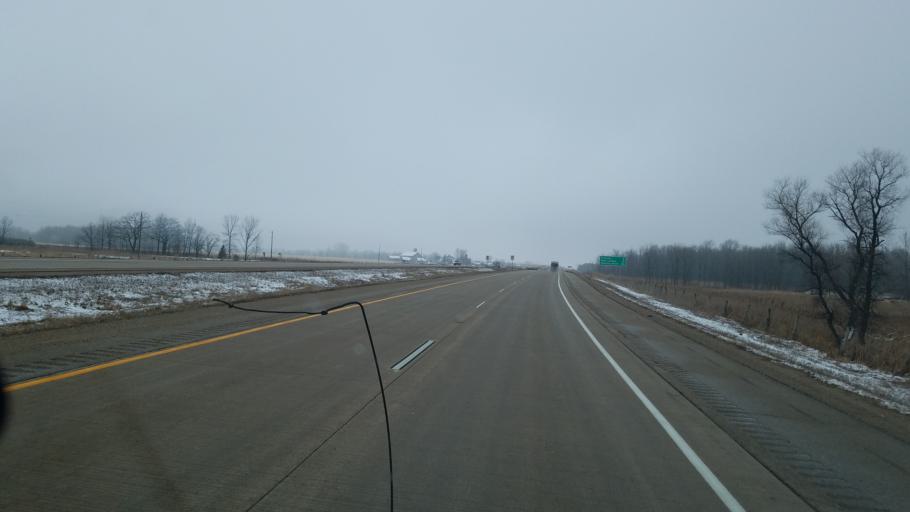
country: US
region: Wisconsin
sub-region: Winnebago County
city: Winneconne
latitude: 44.2140
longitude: -88.6936
